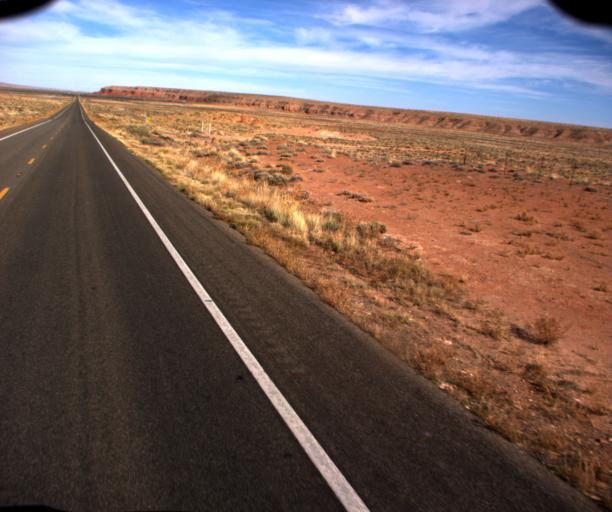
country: US
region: Arizona
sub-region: Navajo County
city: Kayenta
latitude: 36.7446
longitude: -110.0732
